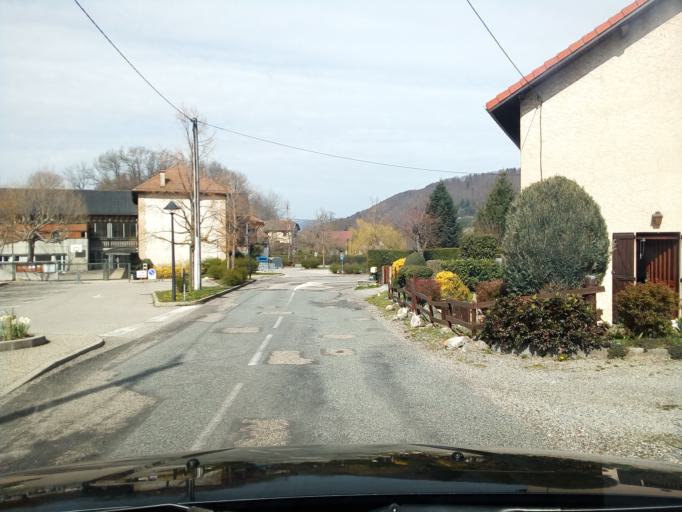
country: FR
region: Rhone-Alpes
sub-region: Departement de l'Isere
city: Revel
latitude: 45.1650
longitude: 5.8503
